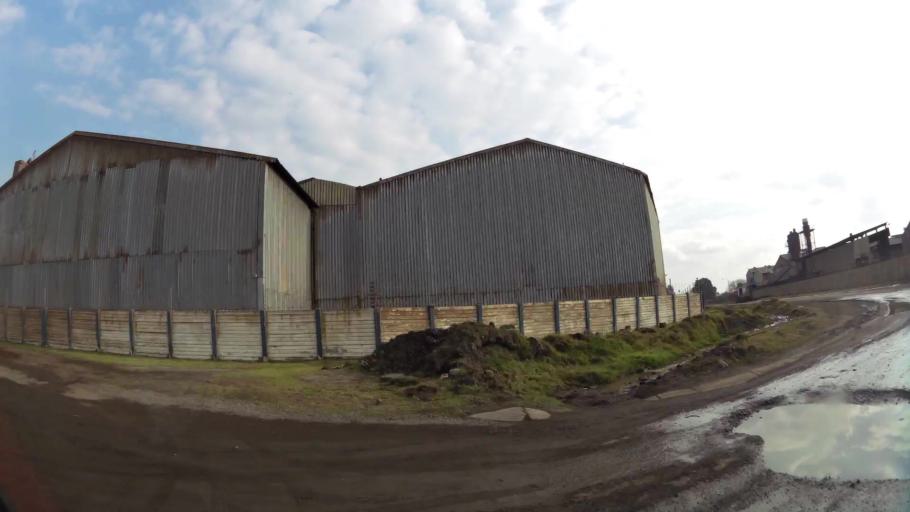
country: ZA
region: Gauteng
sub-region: Sedibeng District Municipality
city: Vereeniging
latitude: -26.6814
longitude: 27.9102
